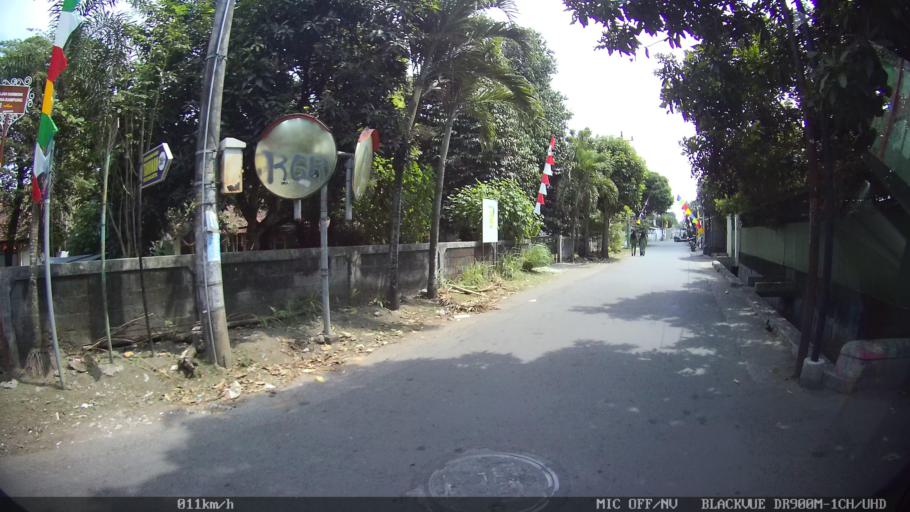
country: ID
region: Daerah Istimewa Yogyakarta
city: Yogyakarta
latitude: -7.8044
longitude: 110.3828
